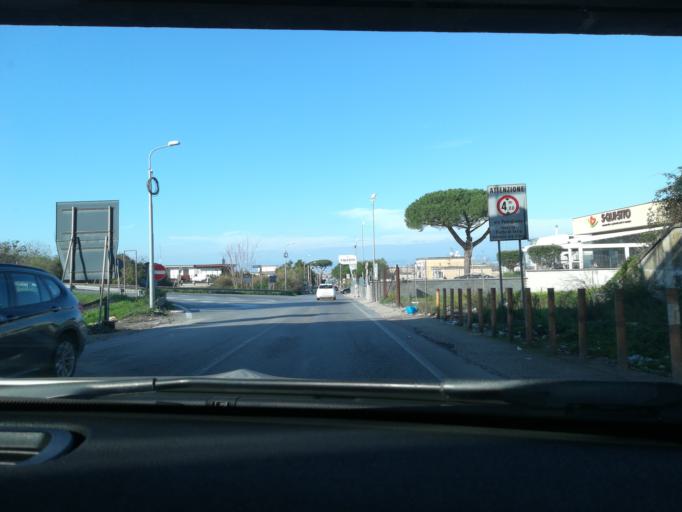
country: IT
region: Campania
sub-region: Provincia di Napoli
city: Sant'Anastasia
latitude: 40.8788
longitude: 14.3988
